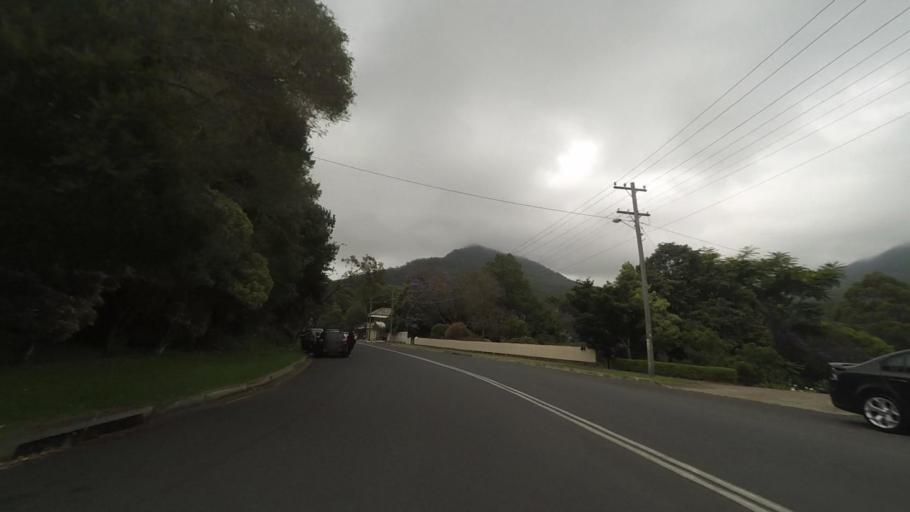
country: AU
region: New South Wales
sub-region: Wollongong
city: Cordeaux Heights
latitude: -34.4313
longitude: 150.8220
